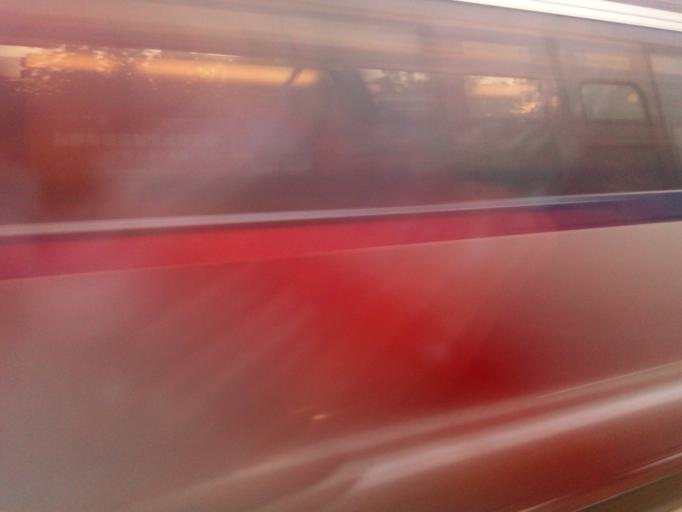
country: HK
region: Tai Po
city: Tai Po
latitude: 22.4940
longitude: 114.1365
